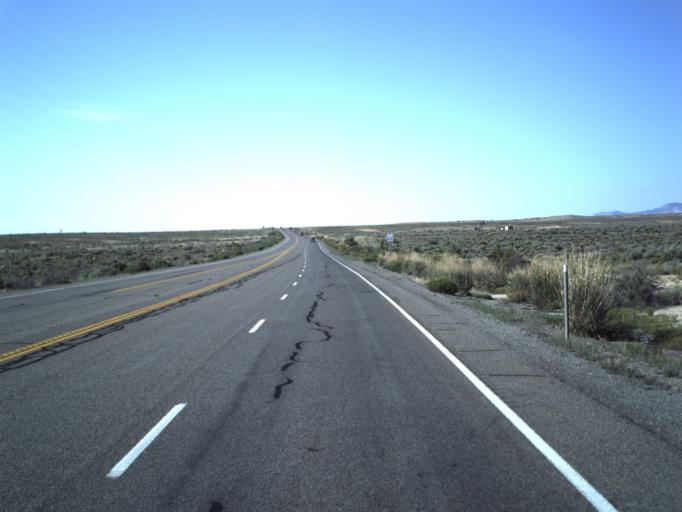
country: US
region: Utah
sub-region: Carbon County
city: Price
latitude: 39.4917
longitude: -110.8467
